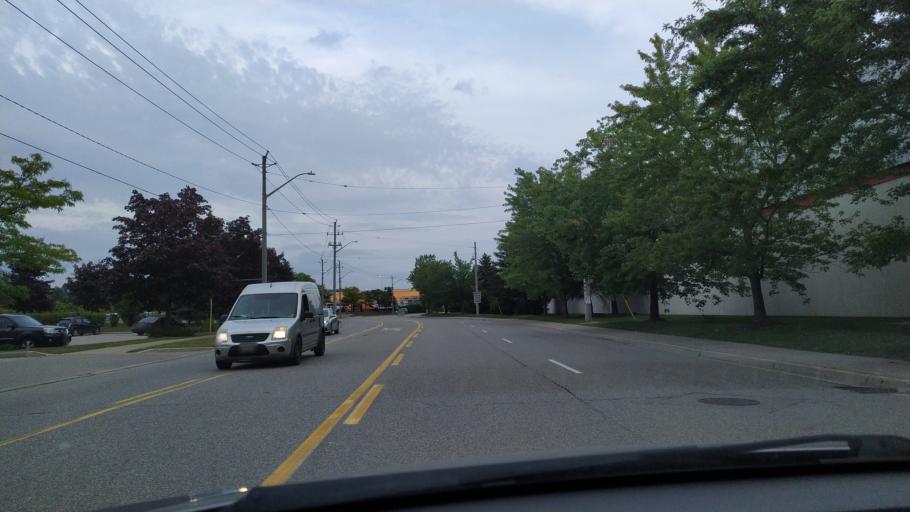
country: CA
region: Ontario
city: Cambridge
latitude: 43.4079
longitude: -80.3920
